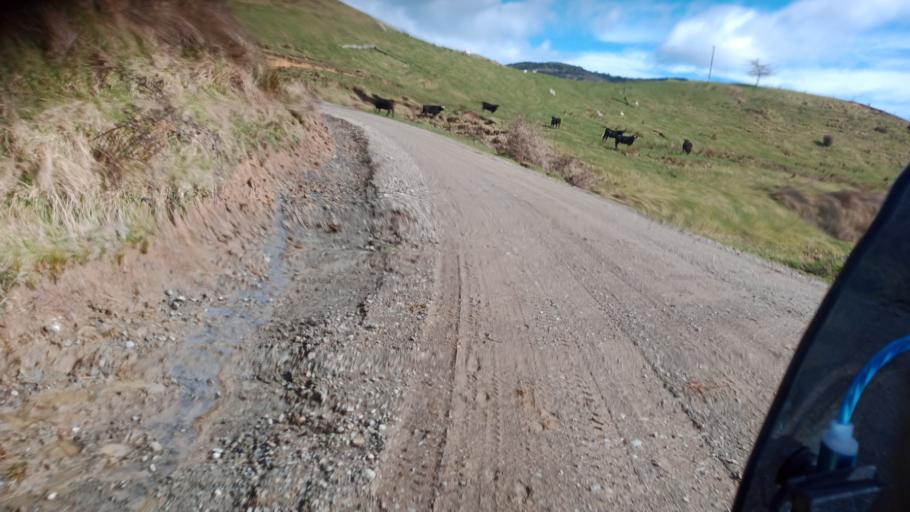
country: NZ
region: Hawke's Bay
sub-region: Wairoa District
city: Wairoa
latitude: -38.7347
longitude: 177.2970
